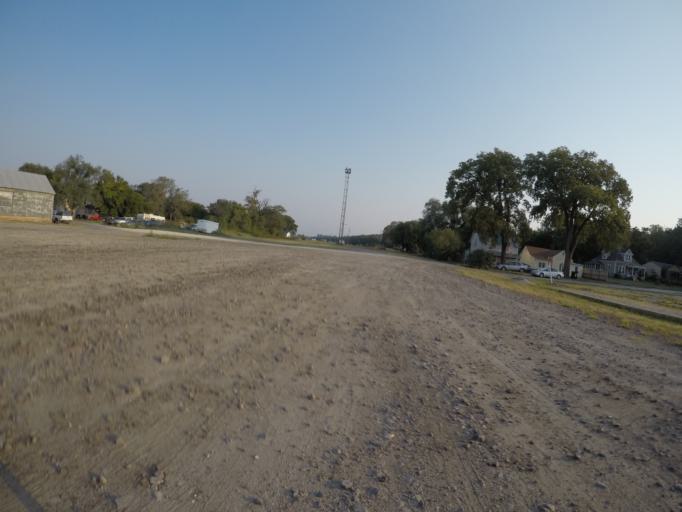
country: US
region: Kansas
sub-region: Marshall County
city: Marysville
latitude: 39.8449
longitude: -96.6494
